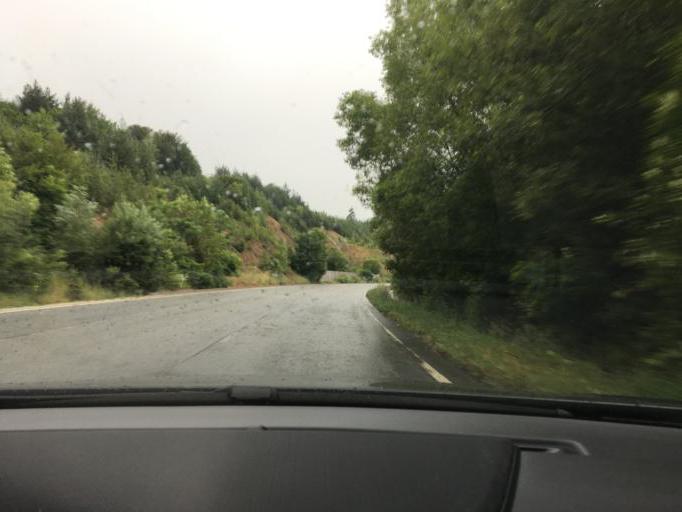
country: BG
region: Kyustendil
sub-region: Obshtina Kyustendil
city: Kyustendil
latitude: 42.2615
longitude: 22.5753
